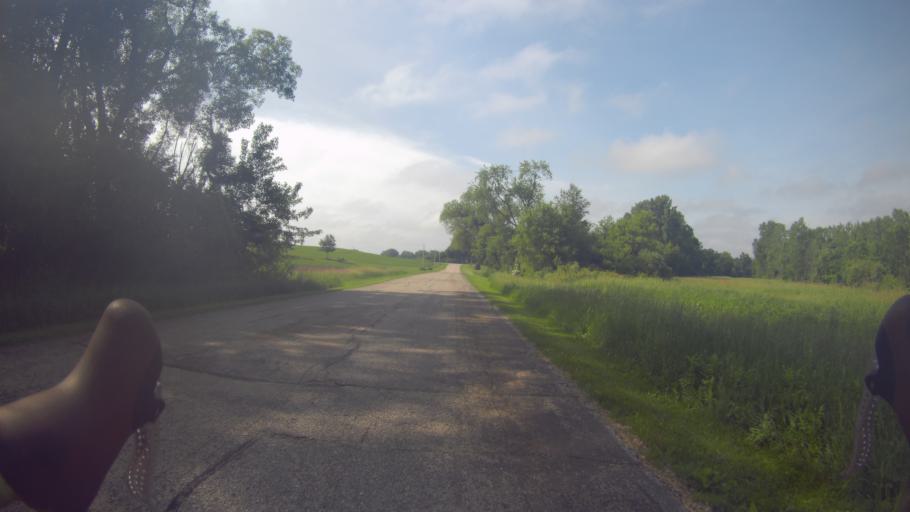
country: US
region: Wisconsin
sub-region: Dane County
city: Stoughton
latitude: 42.9836
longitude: -89.1905
